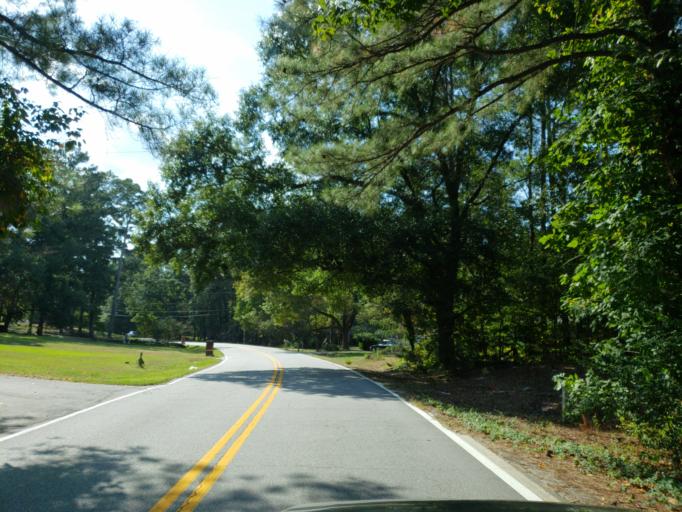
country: US
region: Georgia
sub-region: Cobb County
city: Mableton
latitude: 33.7807
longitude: -84.5405
